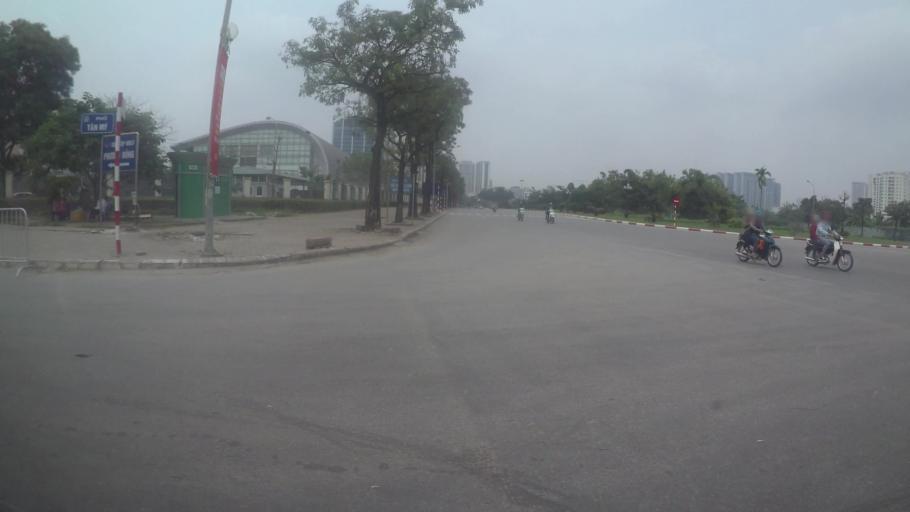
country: VN
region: Ha Noi
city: Cau Dien
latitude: 21.0240
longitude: 105.7665
